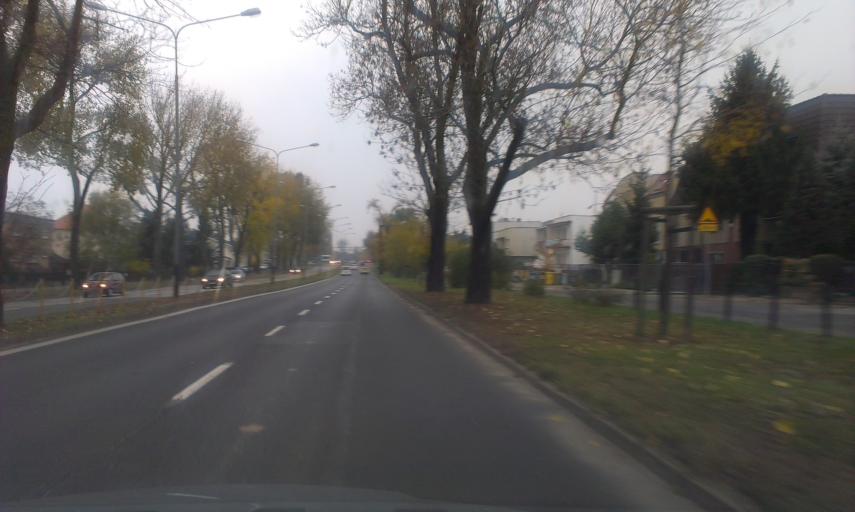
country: PL
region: Greater Poland Voivodeship
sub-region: Powiat poznanski
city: Suchy Las
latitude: 52.4279
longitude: 16.8535
